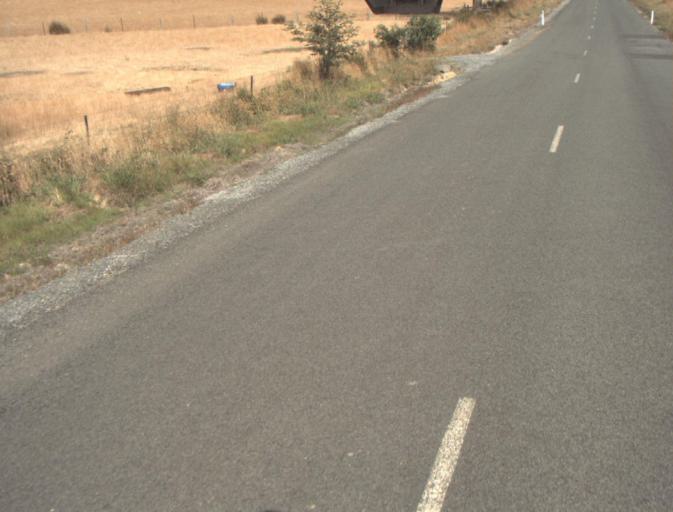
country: AU
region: Tasmania
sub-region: Launceston
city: Mayfield
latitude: -41.2094
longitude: 147.1253
